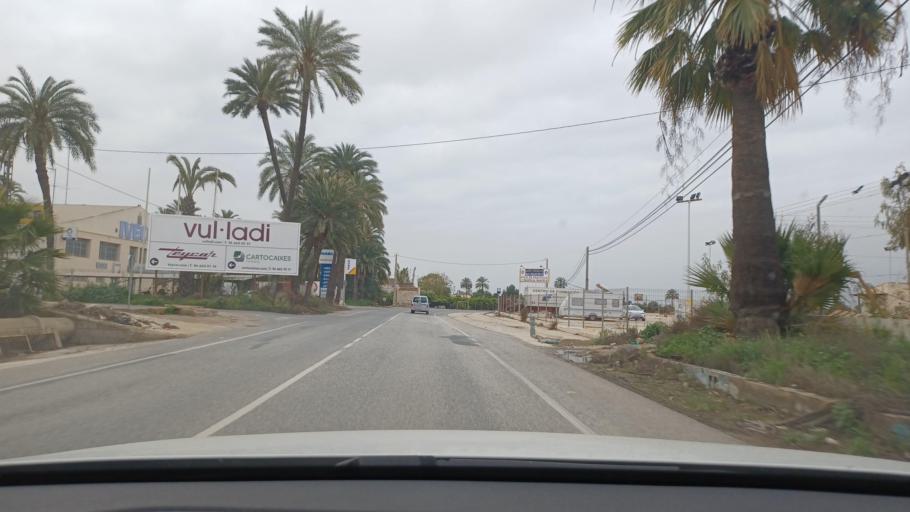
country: ES
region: Valencia
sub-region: Provincia de Alicante
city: Elche
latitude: 38.2401
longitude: -0.7113
